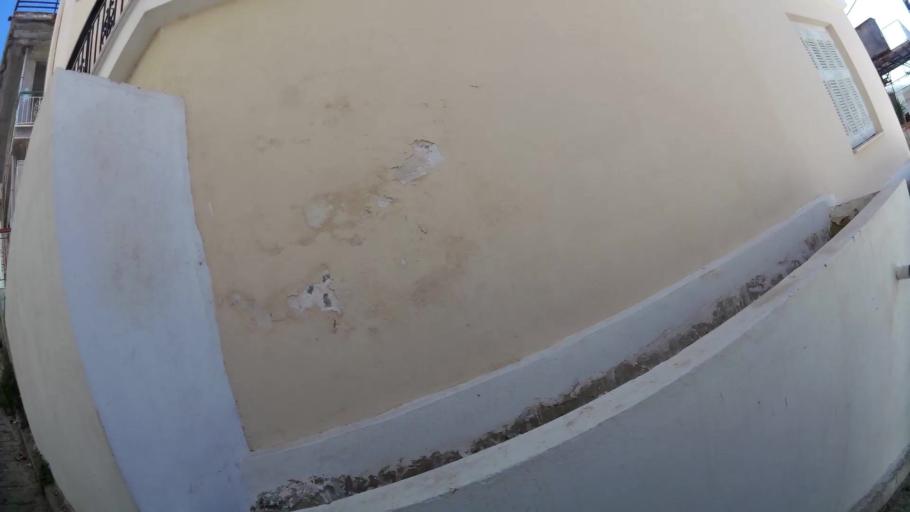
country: GR
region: Attica
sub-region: Nomos Piraios
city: Perama
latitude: 37.9695
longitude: 23.5673
